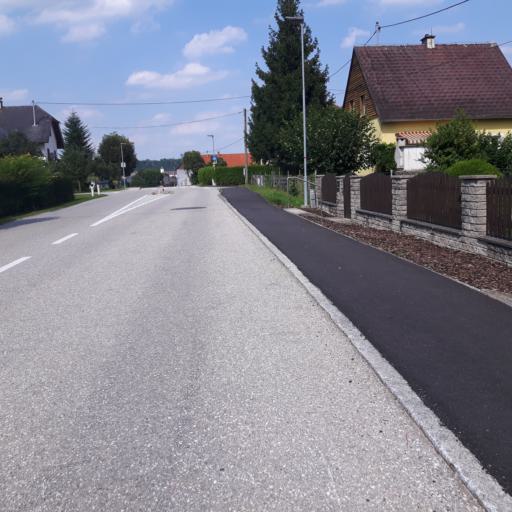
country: AT
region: Upper Austria
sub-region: Wels-Land
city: Stadl-Paura
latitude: 48.0801
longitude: 13.8714
